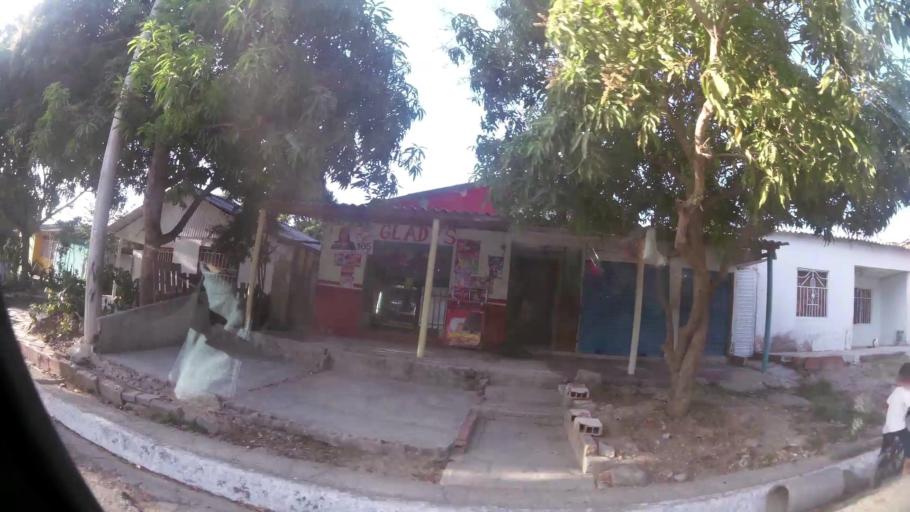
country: CO
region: Atlantico
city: Barranquilla
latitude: 10.9550
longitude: -74.8155
